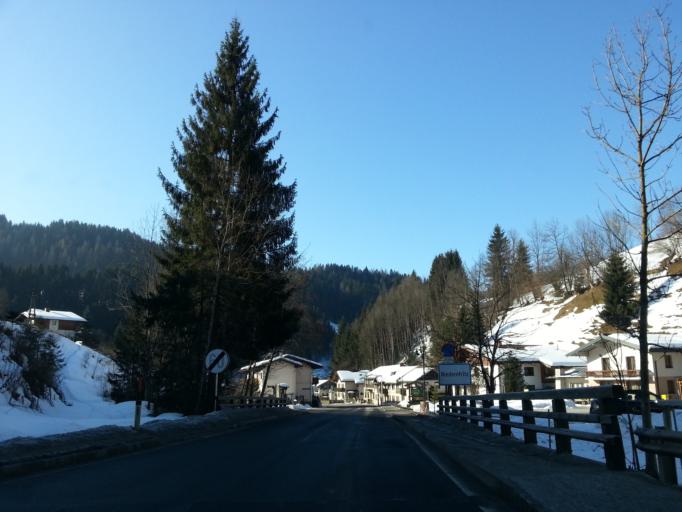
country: AT
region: Salzburg
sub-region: Politischer Bezirk Sankt Johann im Pongau
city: Huttau
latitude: 47.4244
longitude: 13.3467
